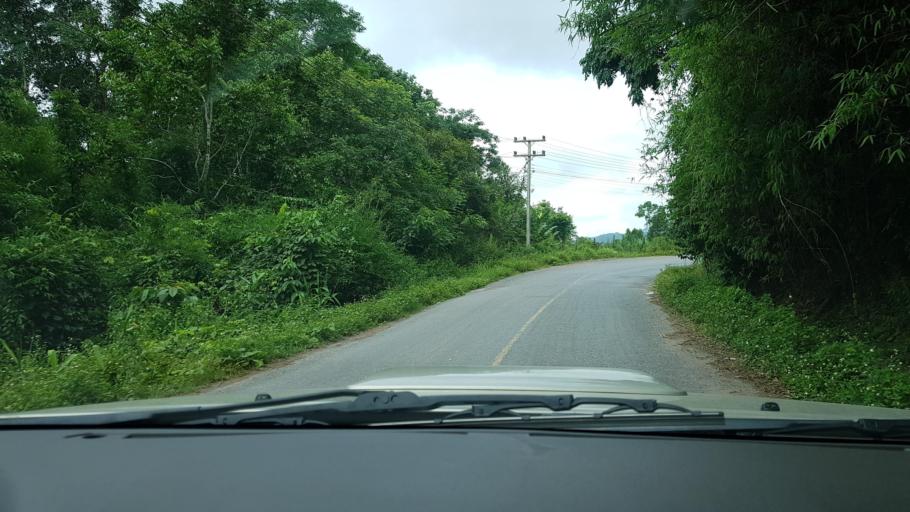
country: LA
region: Oudomxai
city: Muang Xay
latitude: 20.5947
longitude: 101.9384
